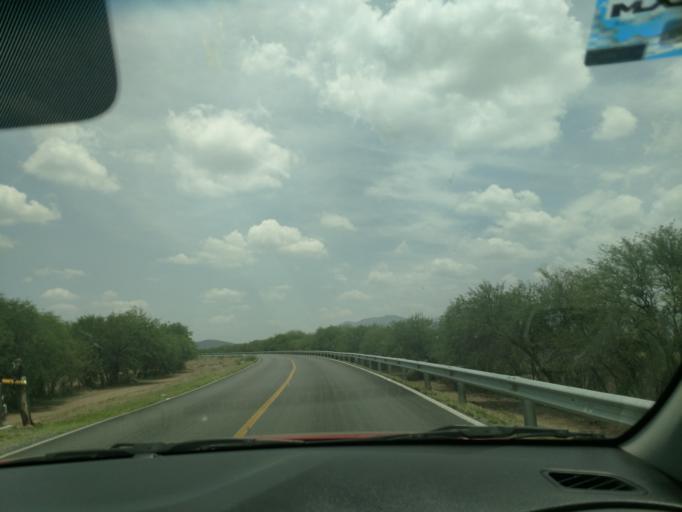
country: MX
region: San Luis Potosi
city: Zaragoza
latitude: 22.0193
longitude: -100.4001
